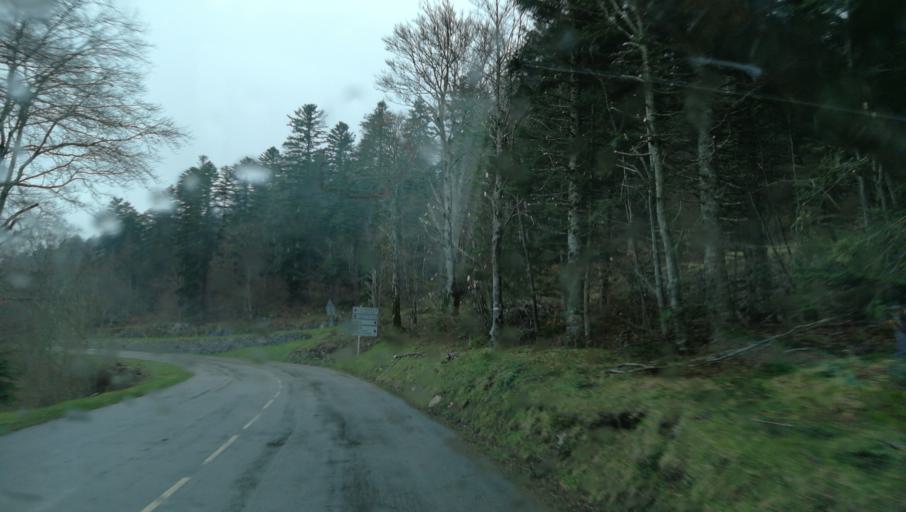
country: FR
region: Rhone-Alpes
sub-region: Departement de la Drome
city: Saint-Laurent-en-Royans
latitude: 44.9673
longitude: 5.3355
